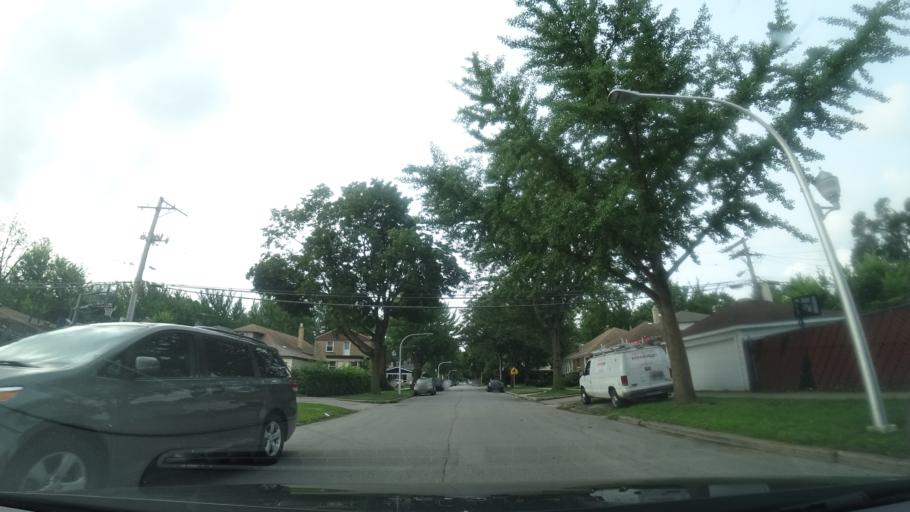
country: US
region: Illinois
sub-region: Cook County
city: Lincolnwood
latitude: 42.0147
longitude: -87.7046
